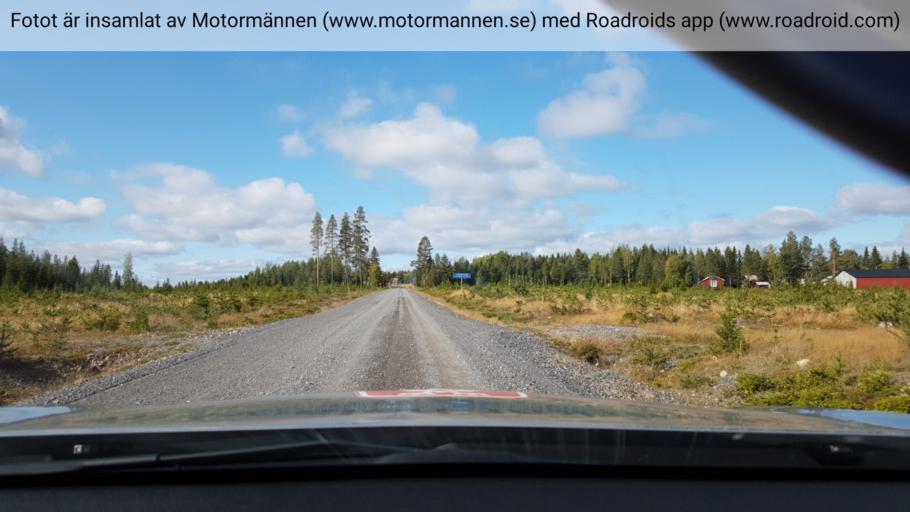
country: SE
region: Vaesterbotten
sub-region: Mala Kommun
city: Mala
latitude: 65.3537
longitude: 18.6875
